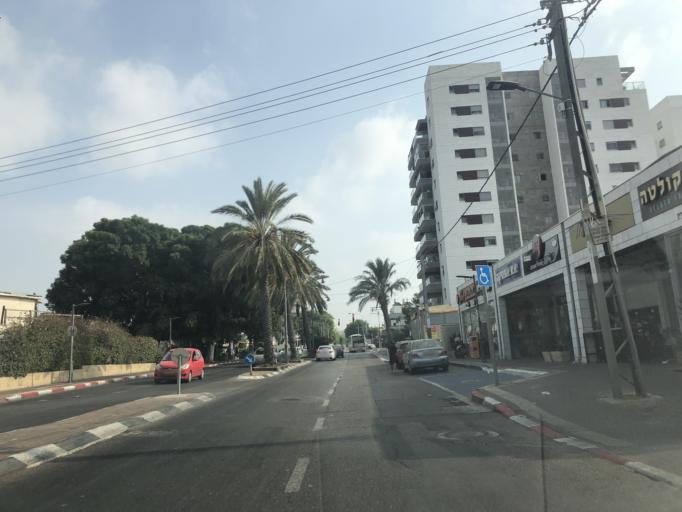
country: IL
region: Central District
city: Rosh Ha'Ayin
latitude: 32.0963
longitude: 34.9438
